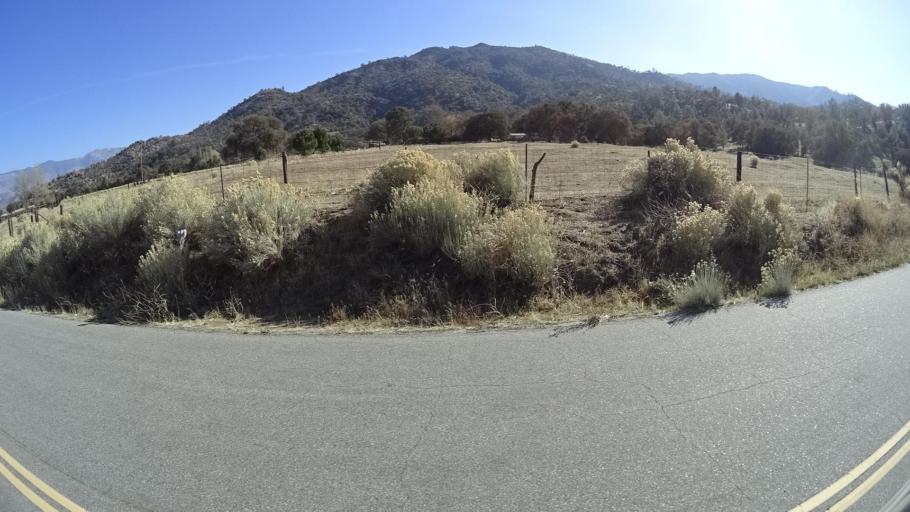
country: US
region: California
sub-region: Kern County
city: Bodfish
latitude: 35.3882
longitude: -118.5348
